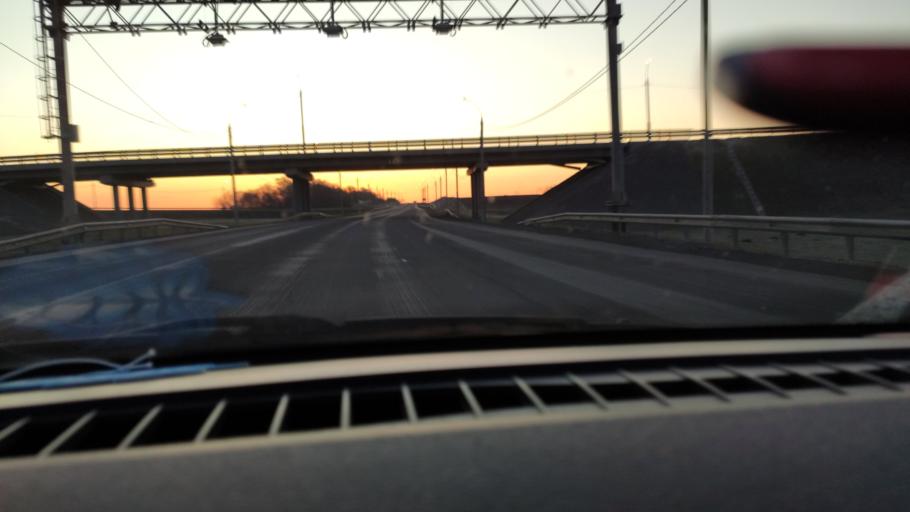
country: RU
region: Saratov
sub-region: Saratovskiy Rayon
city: Saratov
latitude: 51.7744
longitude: 46.0903
